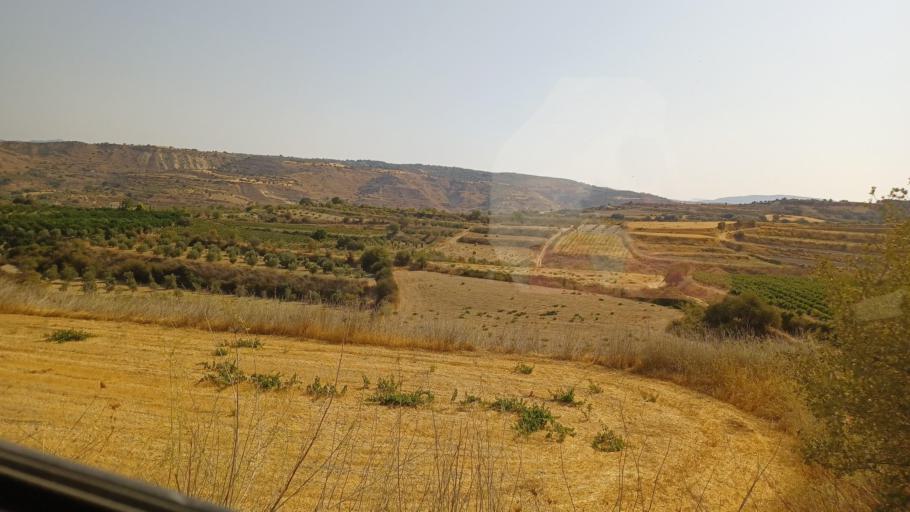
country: CY
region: Pafos
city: Tala
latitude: 34.9065
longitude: 32.4809
